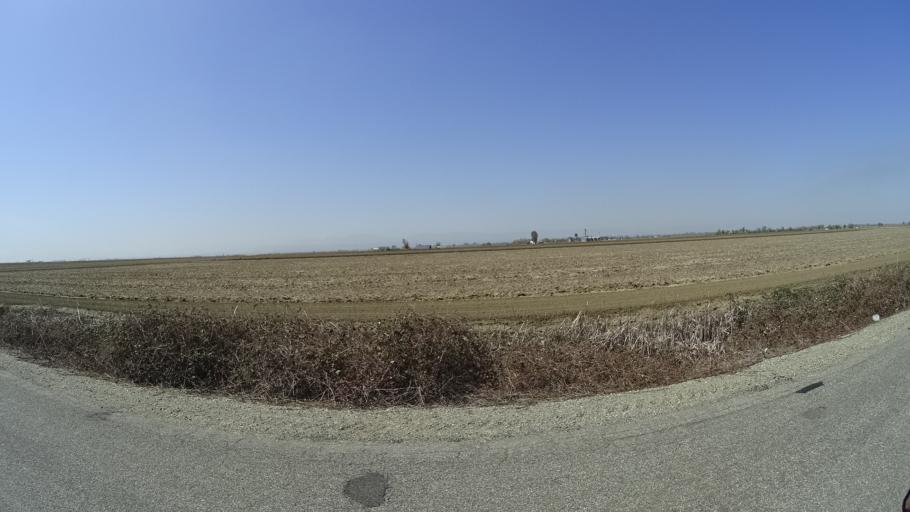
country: US
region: California
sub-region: Glenn County
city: Willows
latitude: 39.5140
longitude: -122.1368
